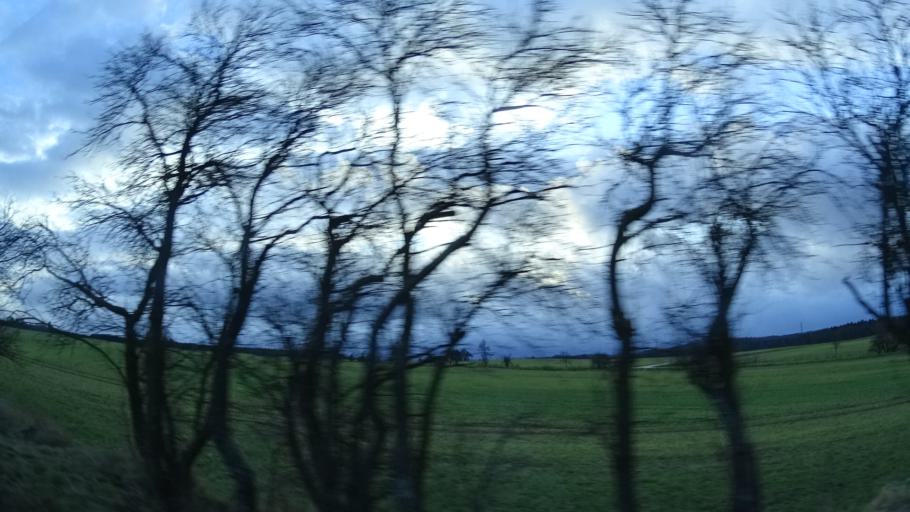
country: DE
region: Thuringia
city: Behringen
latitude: 50.7310
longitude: 11.0361
